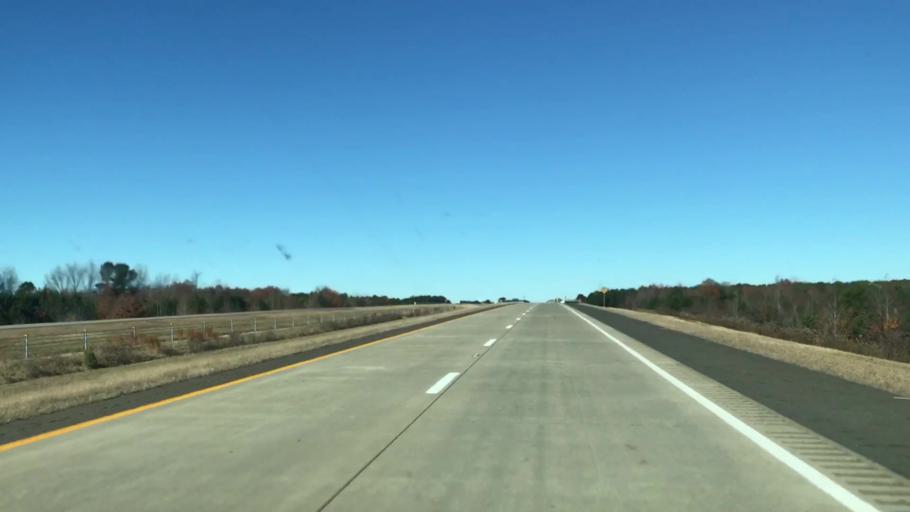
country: US
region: Texas
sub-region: Bowie County
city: Texarkana
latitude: 33.2486
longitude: -93.8836
